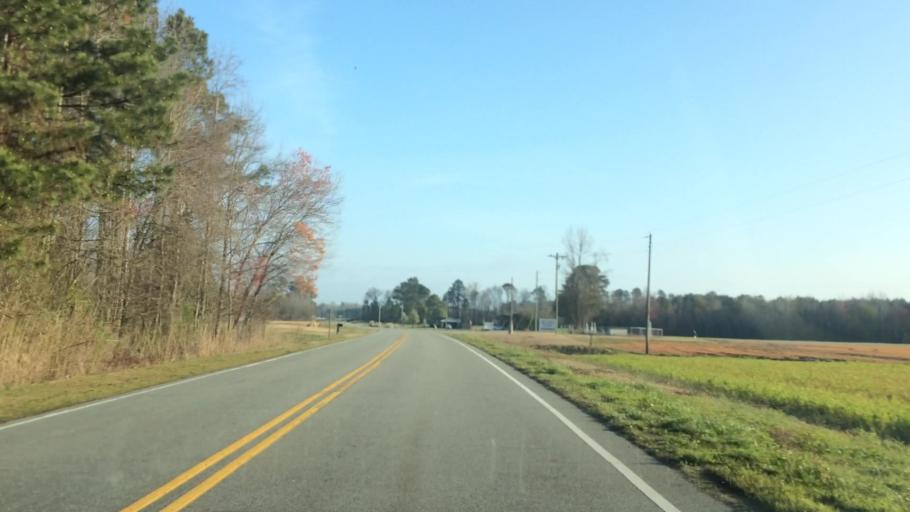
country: US
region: North Carolina
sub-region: Edgecombe County
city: Pinetops
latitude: 35.7033
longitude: -77.6337
